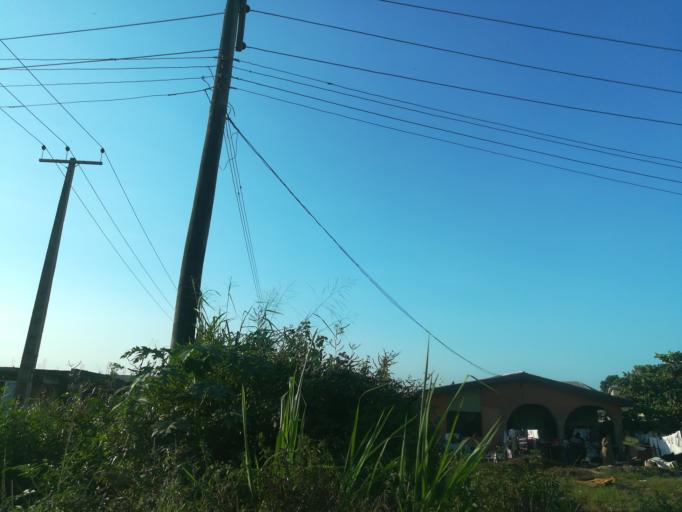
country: NG
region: Lagos
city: Ikorodu
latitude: 6.5912
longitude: 3.5126
